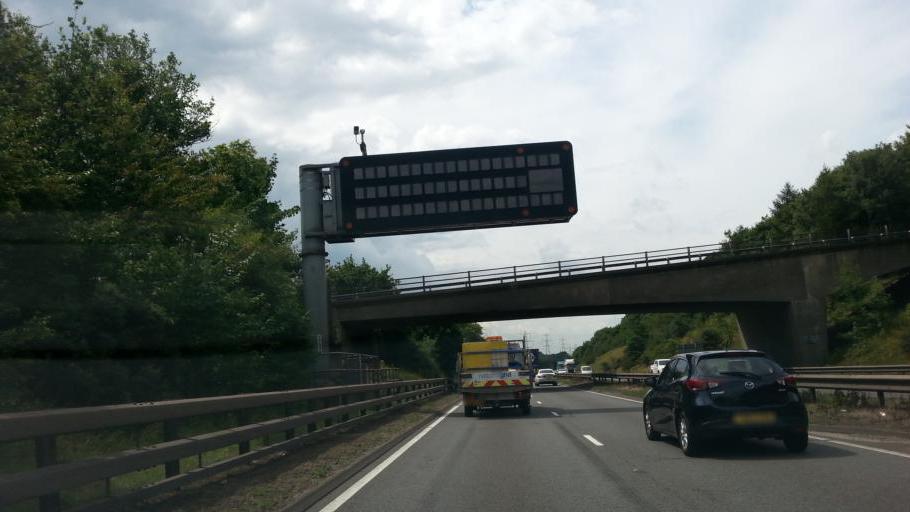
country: GB
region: England
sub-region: Staffordshire
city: Lichfield
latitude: 52.6770
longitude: -1.7990
